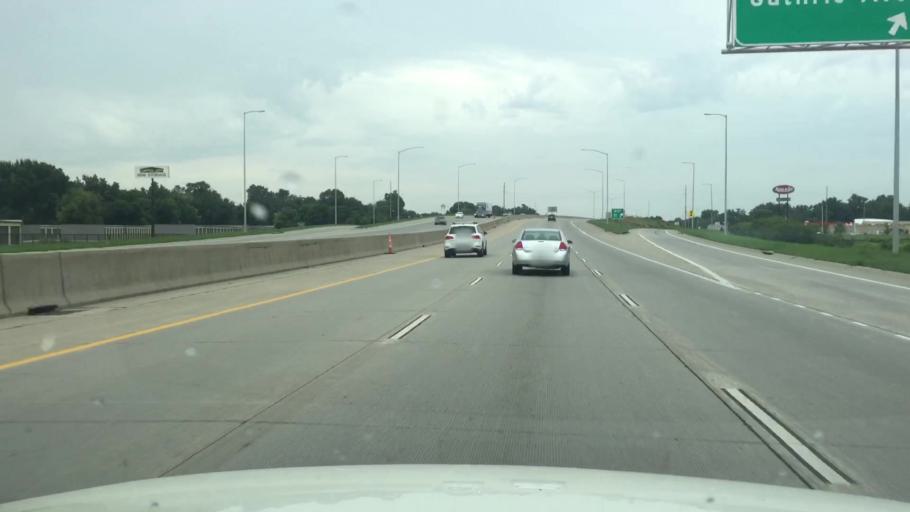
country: US
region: Iowa
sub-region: Polk County
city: Des Moines
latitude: 41.6188
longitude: -93.5767
